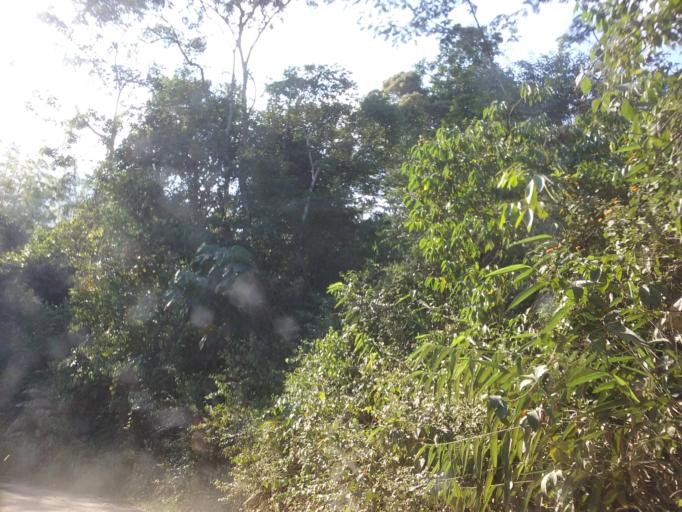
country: CO
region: Tolima
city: Libano
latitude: 4.8950
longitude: -75.0308
